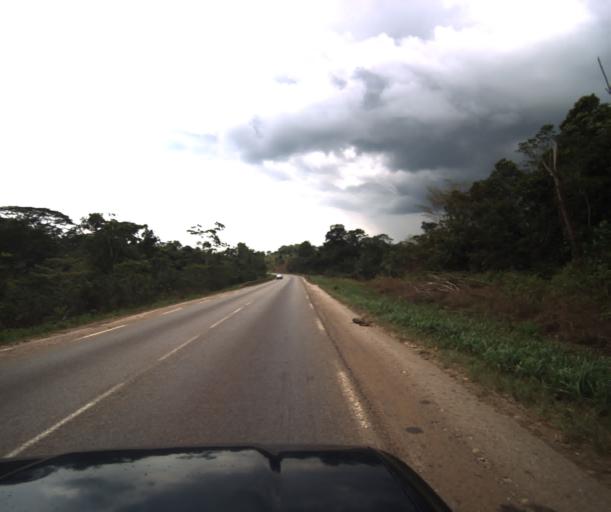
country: CM
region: Littoral
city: Dizangue
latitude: 3.9500
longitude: 10.0174
